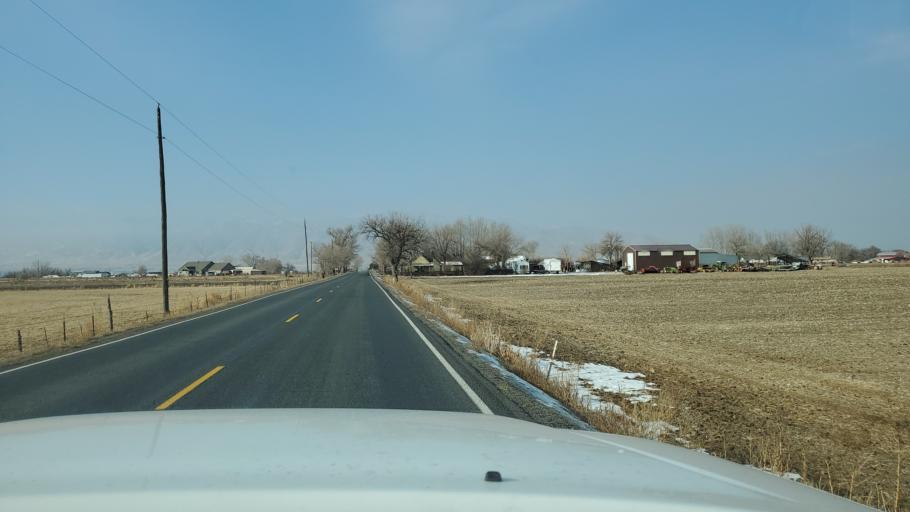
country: US
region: Utah
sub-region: Utah County
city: Benjamin
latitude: 40.0853
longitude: -111.7235
